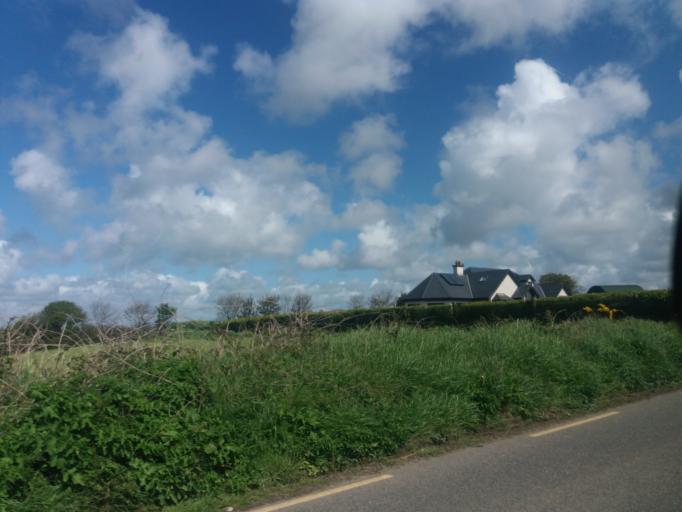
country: IE
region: Leinster
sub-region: Loch Garman
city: New Ross
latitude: 52.2623
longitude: -6.7925
